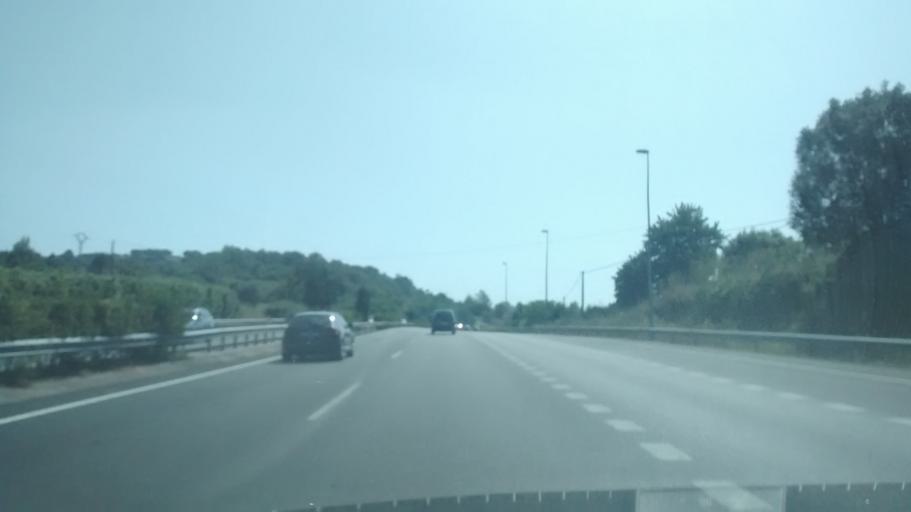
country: ES
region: Cantabria
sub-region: Provincia de Cantabria
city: Laredo
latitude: 43.4035
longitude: -3.4085
